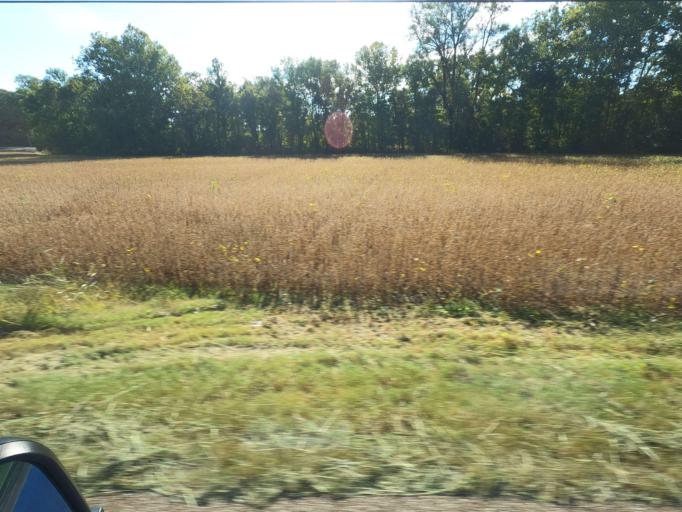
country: US
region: Tennessee
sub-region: Tipton County
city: Brighton
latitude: 35.5212
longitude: -89.6953
